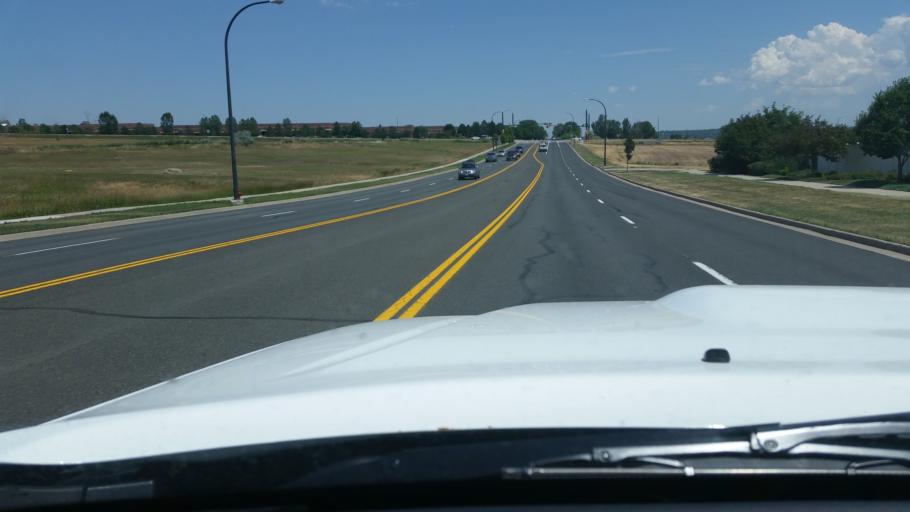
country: US
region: Colorado
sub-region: Broomfield County
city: Broomfield
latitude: 39.8927
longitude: -105.1000
